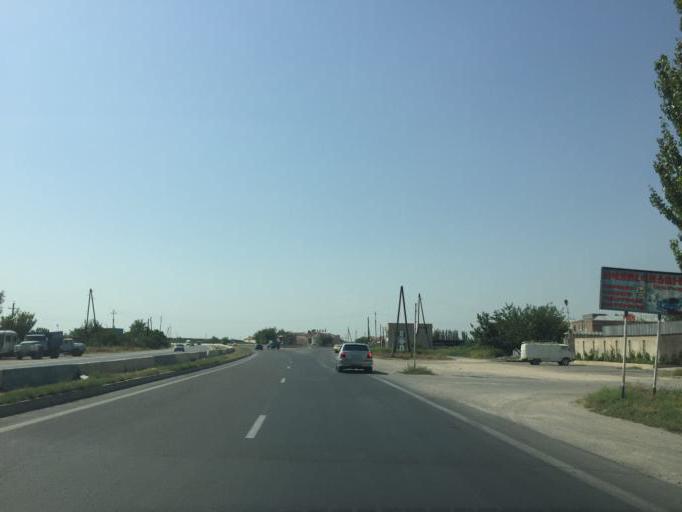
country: AM
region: Ararat
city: Artashat
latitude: 39.9546
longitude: 44.5371
